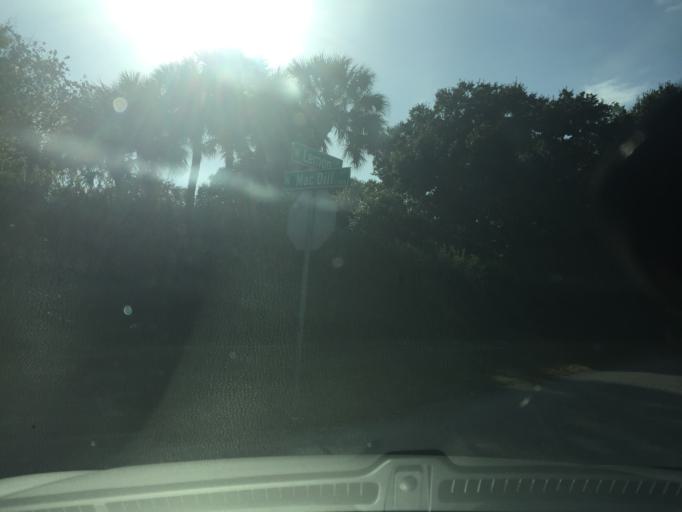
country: US
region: Florida
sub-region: Hillsborough County
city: Tampa
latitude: 27.9509
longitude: -82.4934
